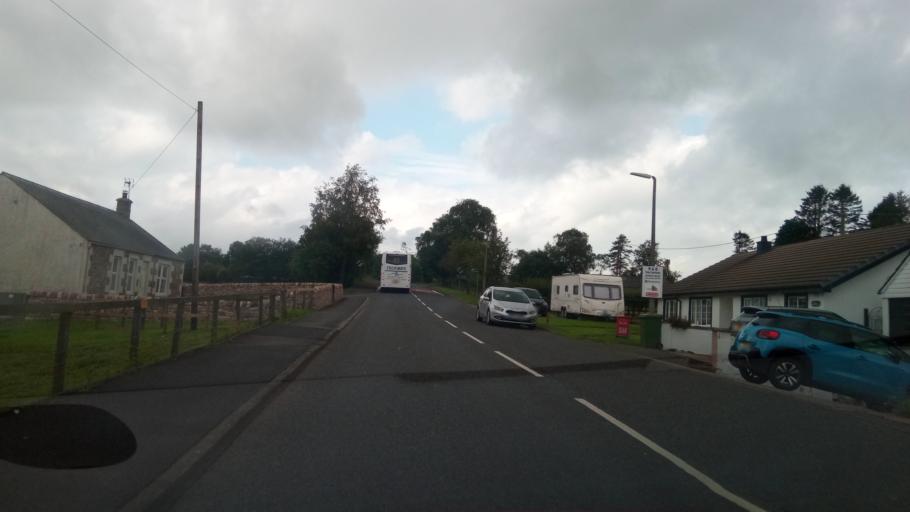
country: GB
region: Scotland
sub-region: Dumfries and Galloway
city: Langholm
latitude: 55.0852
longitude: -2.9289
